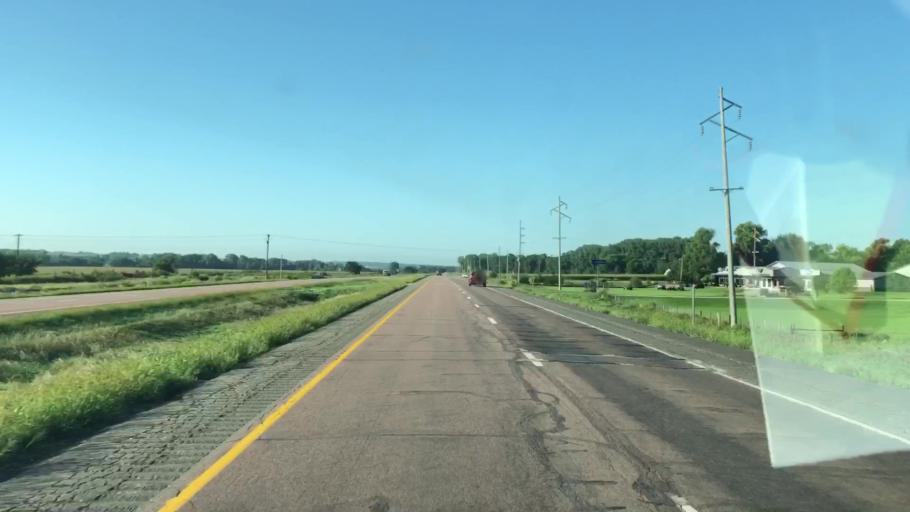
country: US
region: Iowa
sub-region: Woodbury County
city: Sioux City
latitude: 42.5960
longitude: -96.3043
